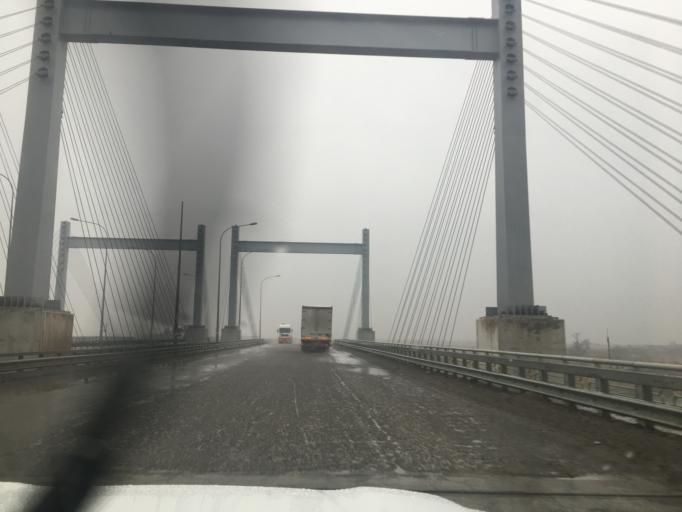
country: TM
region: Ahal
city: Tejen
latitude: 37.2348
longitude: 60.8583
